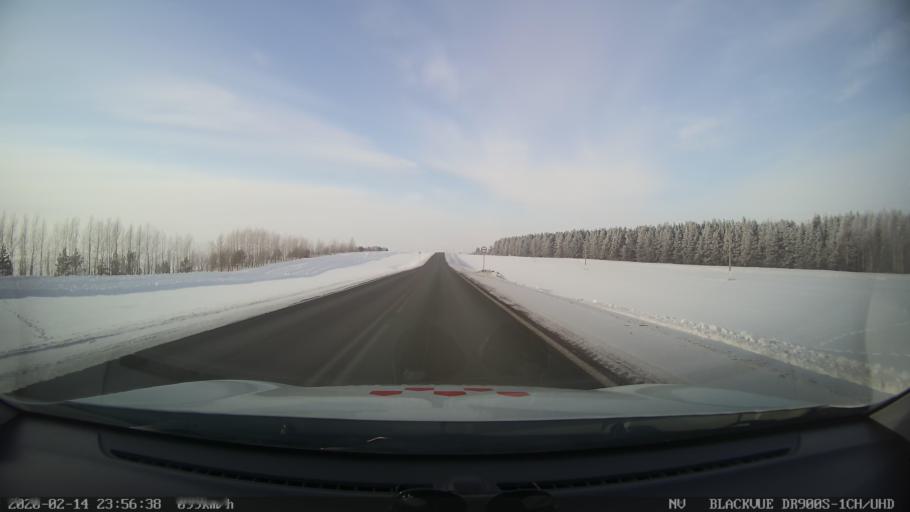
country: RU
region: Tatarstan
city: Kuybyshevskiy Zaton
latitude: 55.3269
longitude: 49.1266
